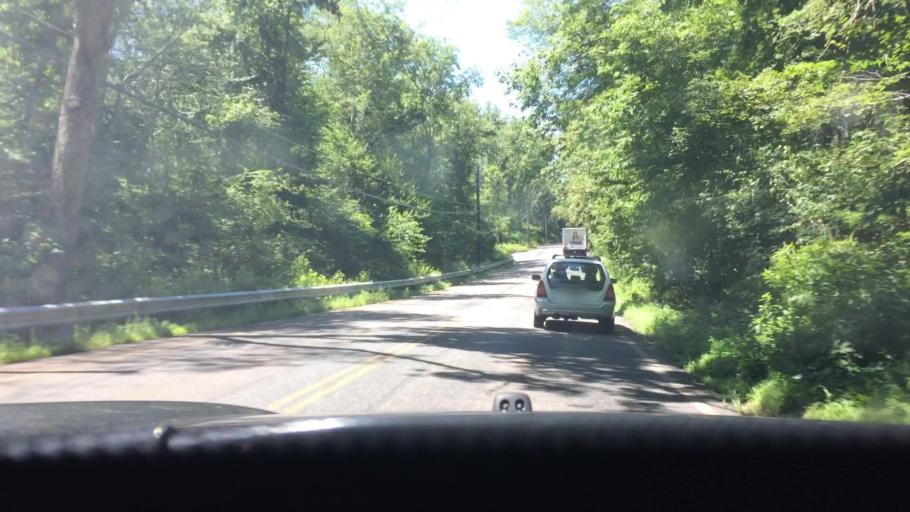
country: US
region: Rhode Island
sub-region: Providence County
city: Harrisville
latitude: 42.0219
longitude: -71.6666
